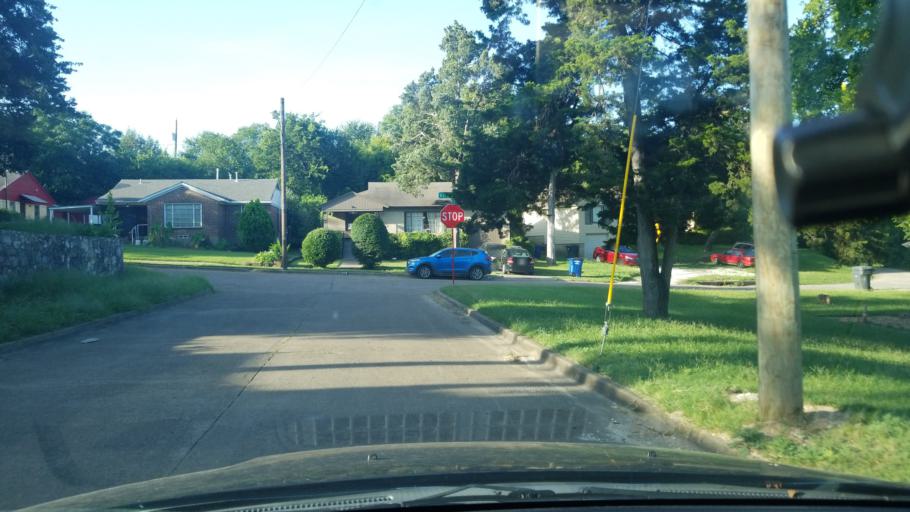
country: US
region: Texas
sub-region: Dallas County
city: Dallas
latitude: 32.7285
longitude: -96.8192
